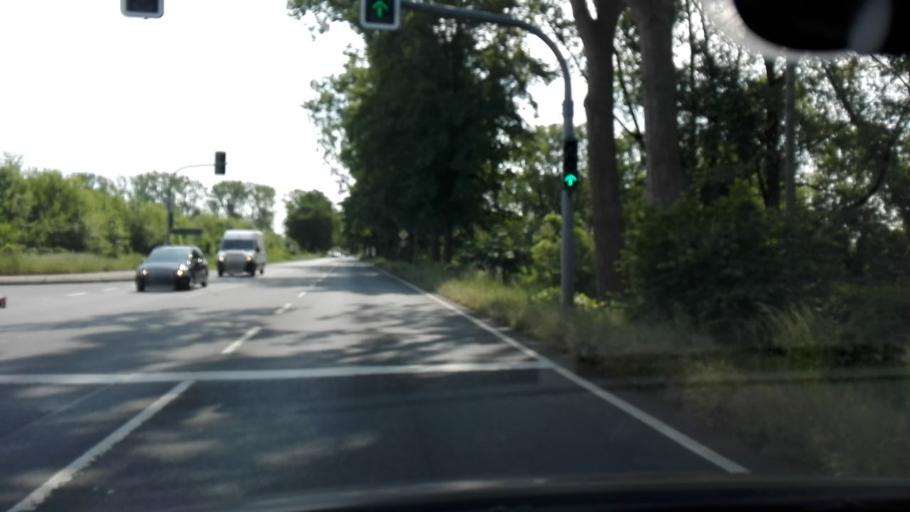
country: DE
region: North Rhine-Westphalia
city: Bergkamen
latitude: 51.5909
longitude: 7.6229
